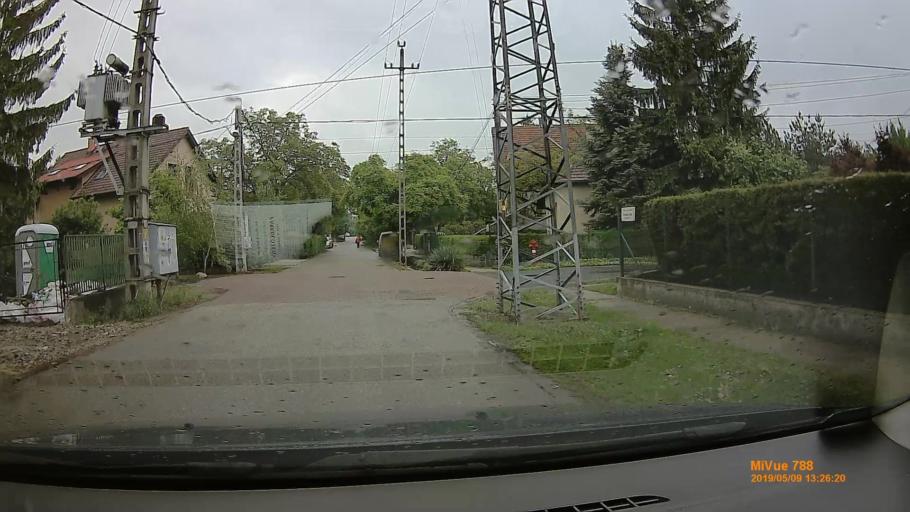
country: HU
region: Budapest
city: Budapest XVI. keruelet
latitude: 47.5367
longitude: 19.1892
